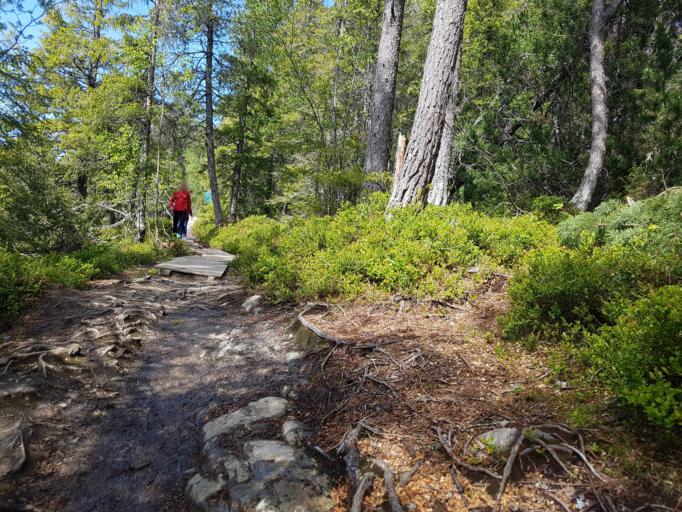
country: NO
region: Sor-Trondelag
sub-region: Trondheim
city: Trondheim
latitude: 63.4288
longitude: 10.3057
